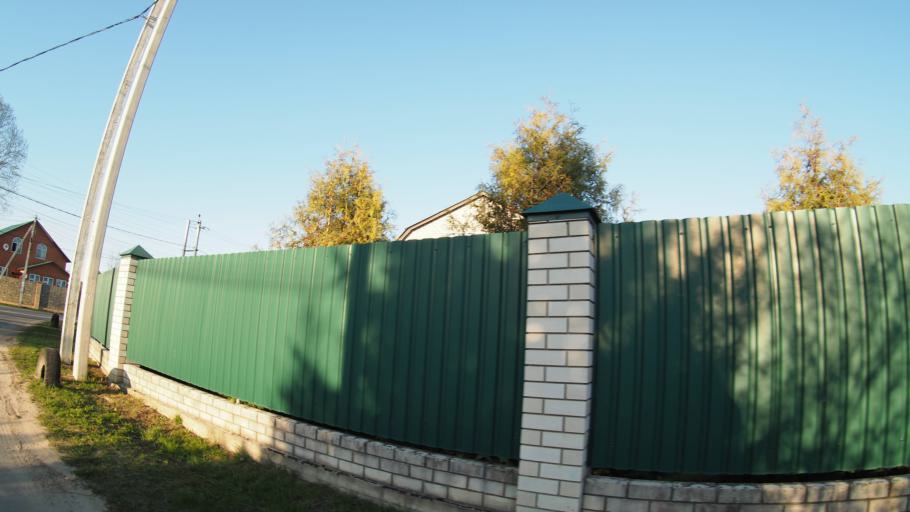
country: RU
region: Moskovskaya
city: Malyshevo
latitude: 55.4975
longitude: 38.3453
